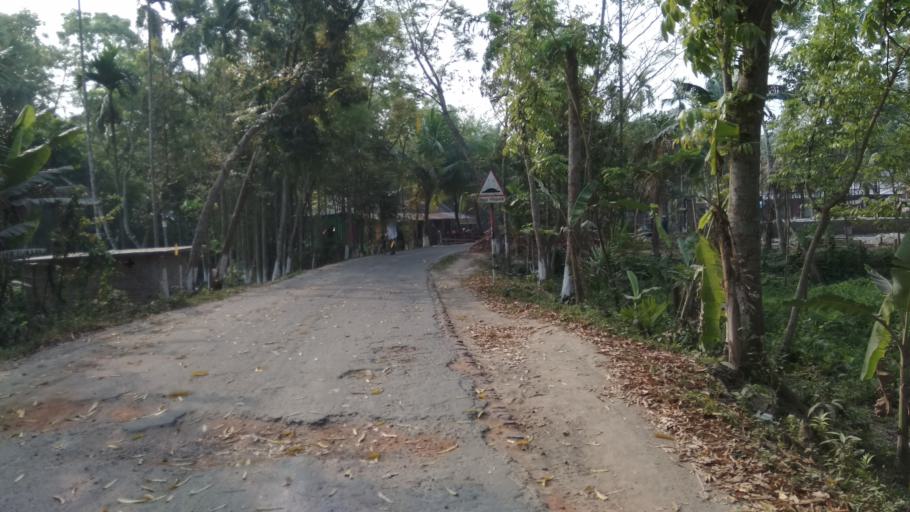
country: BD
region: Barisal
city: Mehendiganj
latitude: 22.9545
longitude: 90.4153
